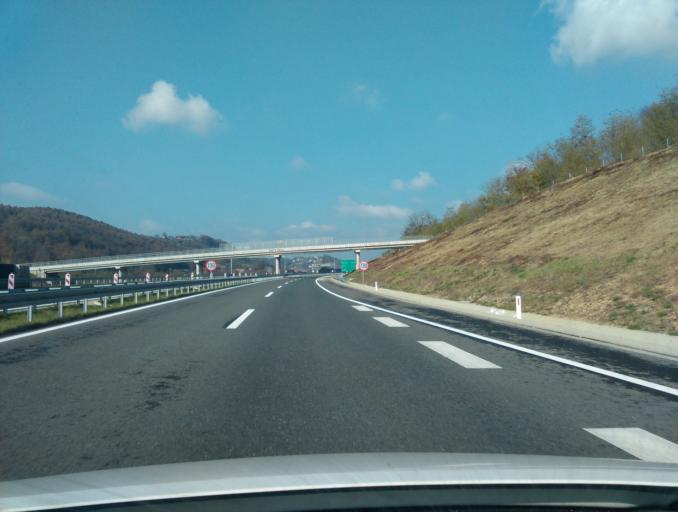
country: BA
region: Republika Srpska
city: Doboj
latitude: 44.8127
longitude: 18.0359
